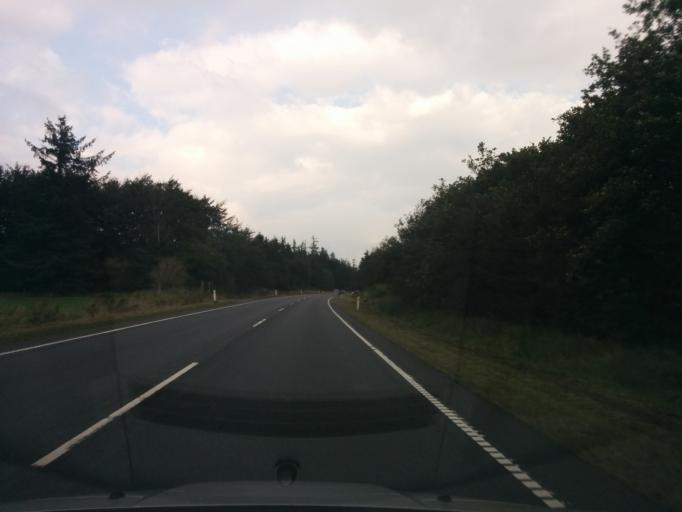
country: DK
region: South Denmark
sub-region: Esbjerg Kommune
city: Bramming
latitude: 55.6317
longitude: 8.7765
